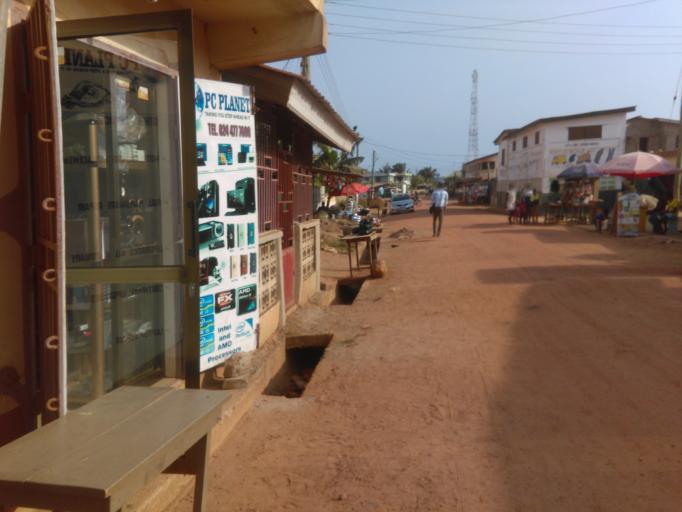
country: GH
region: Central
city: Cape Coast
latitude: 5.1111
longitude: -1.2945
